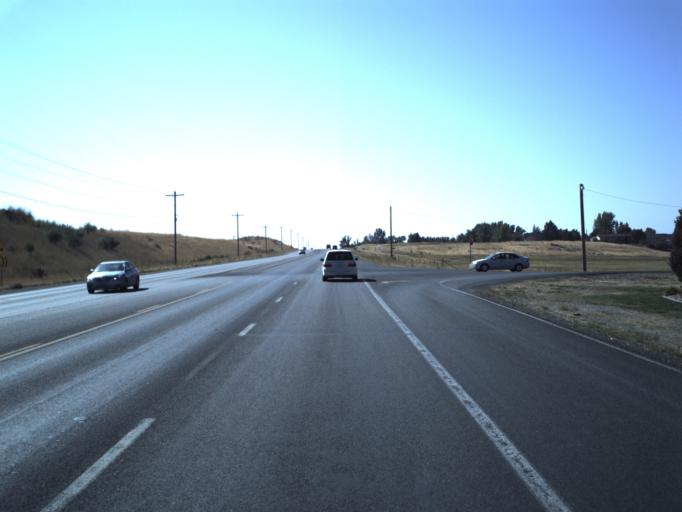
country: US
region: Utah
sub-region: Cache County
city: Hyrum
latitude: 41.6487
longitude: -111.8329
